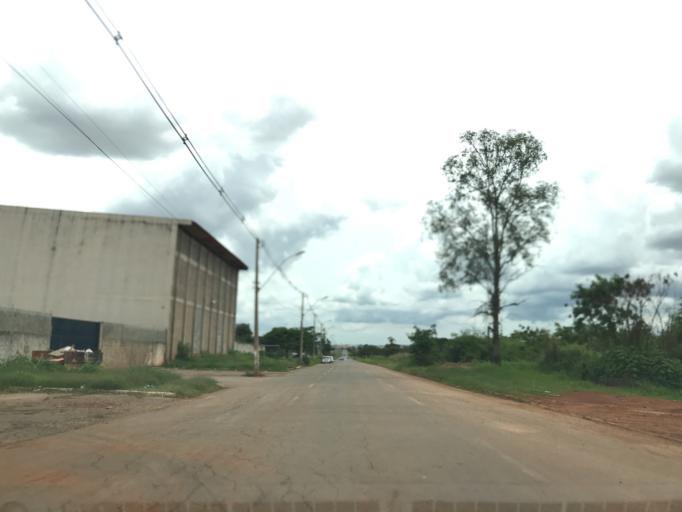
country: BR
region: Federal District
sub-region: Brasilia
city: Brasilia
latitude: -15.7934
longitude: -47.9906
